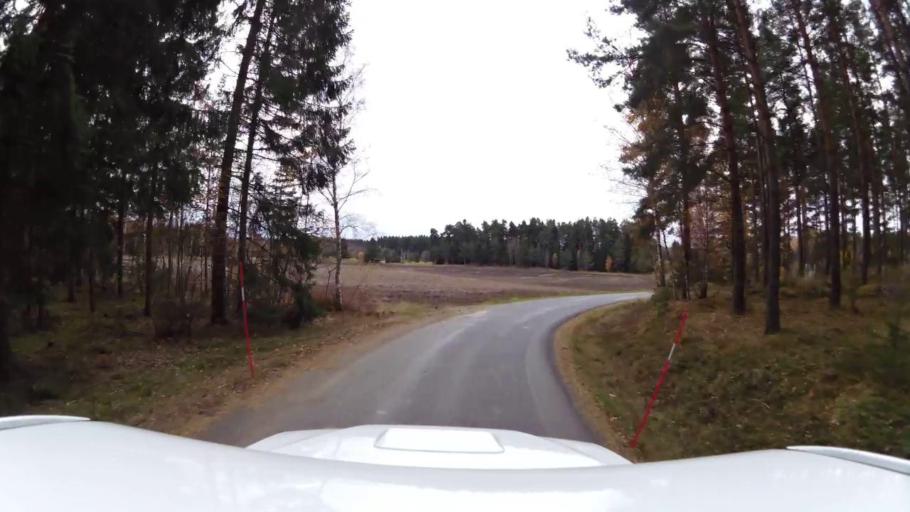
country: SE
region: OEstergoetland
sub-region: Linkopings Kommun
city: Linghem
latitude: 58.4024
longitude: 15.8448
